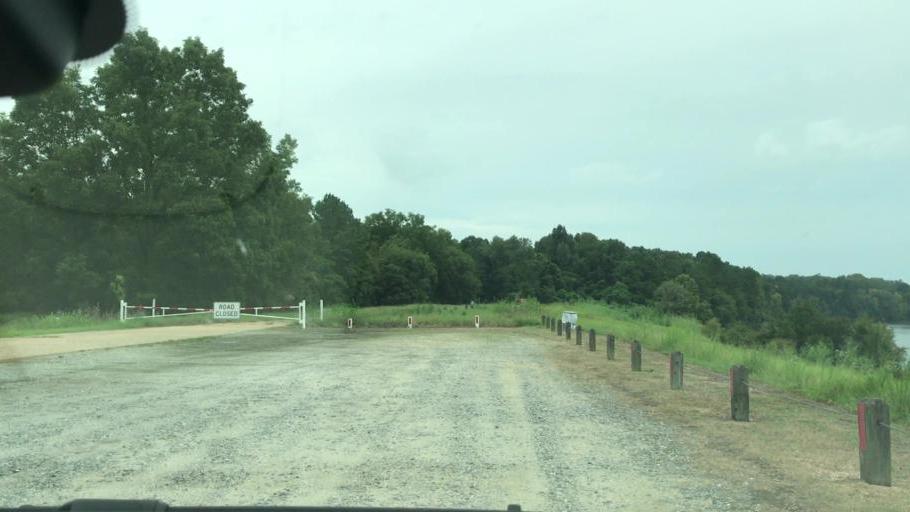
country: US
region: Georgia
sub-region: Clay County
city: Fort Gaines
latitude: 31.6241
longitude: -85.0590
